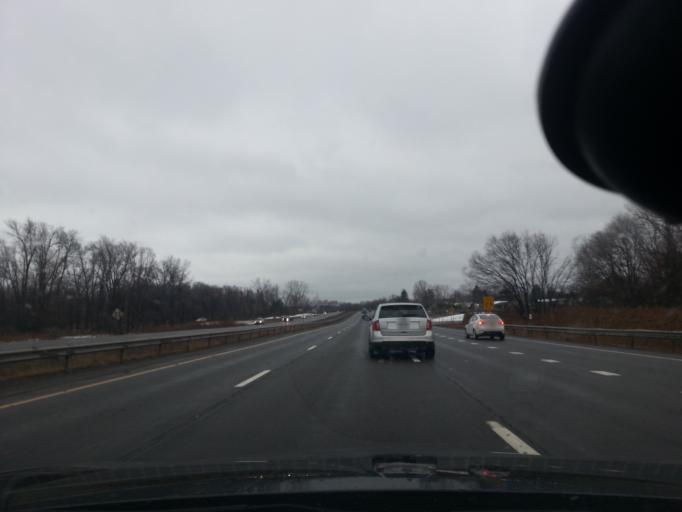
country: US
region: New York
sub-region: Onondaga County
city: North Syracuse
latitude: 43.1405
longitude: -76.1139
